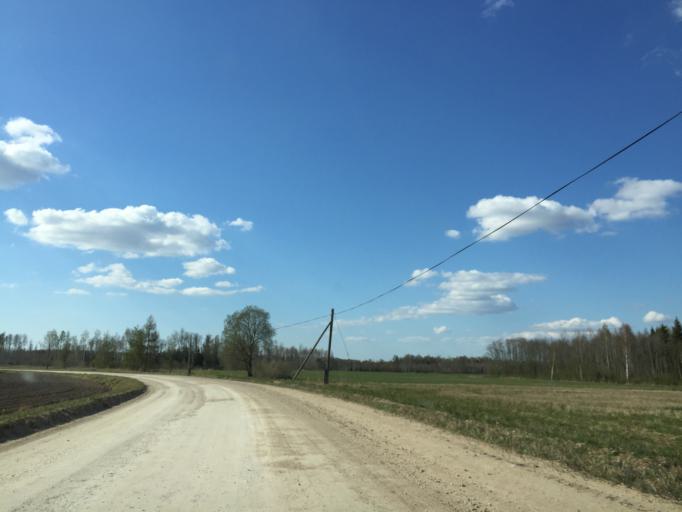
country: LV
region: Saulkrastu
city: Saulkrasti
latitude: 57.3497
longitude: 24.5774
